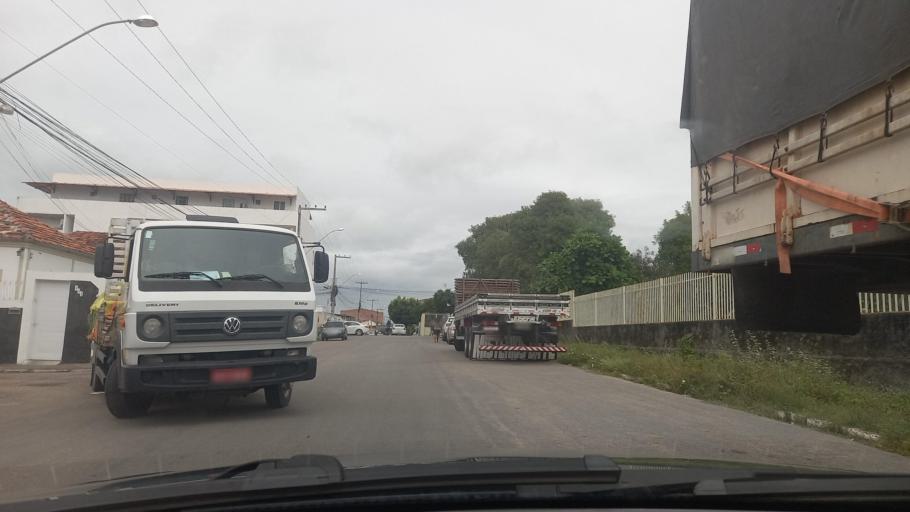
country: BR
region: Alagoas
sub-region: Delmiro Gouveia
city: Delmiro Gouveia
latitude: -9.3864
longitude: -37.9974
